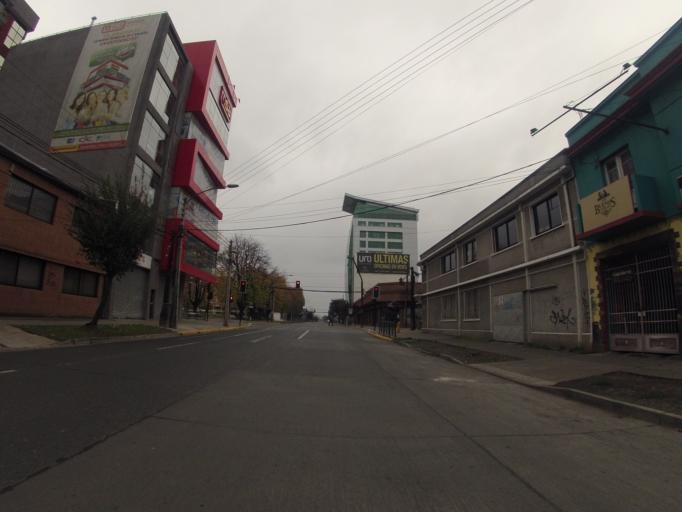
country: CL
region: Araucania
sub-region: Provincia de Cautin
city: Temuco
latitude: -38.7426
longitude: -72.5909
